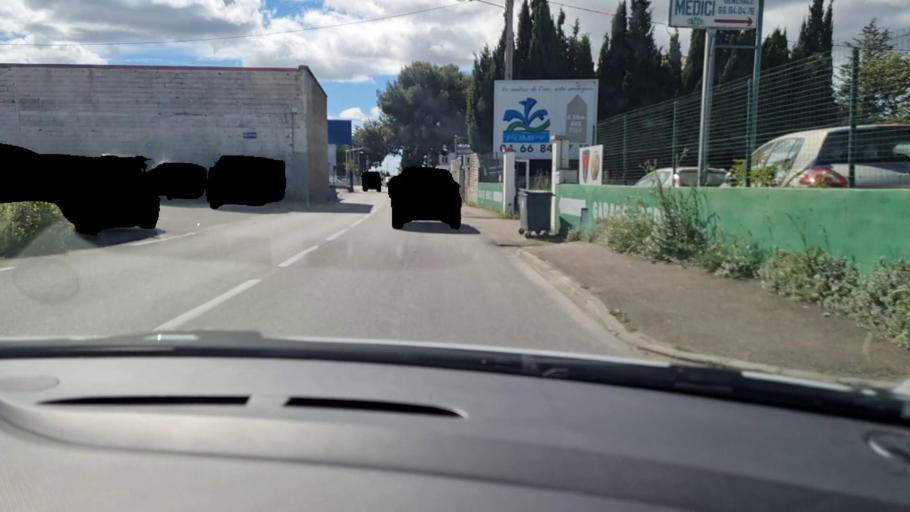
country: FR
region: Languedoc-Roussillon
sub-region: Departement du Gard
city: Milhaud
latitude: 43.8118
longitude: 4.3296
